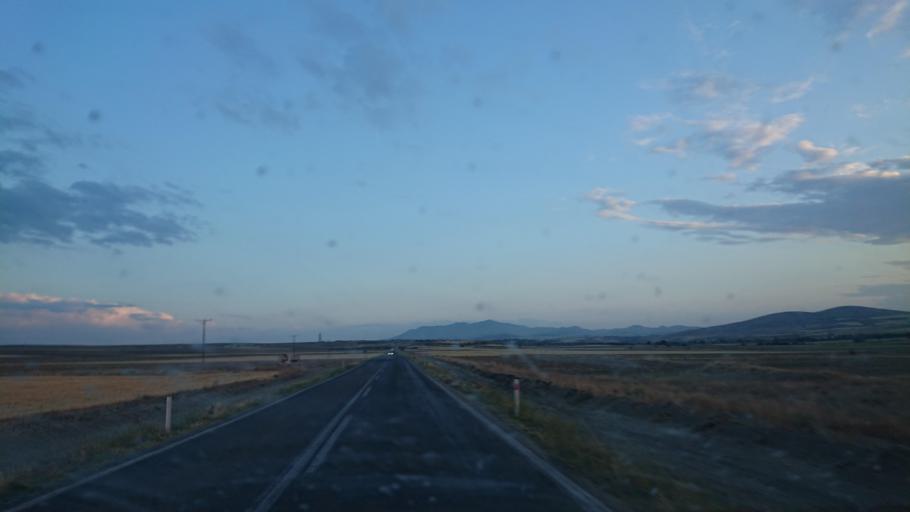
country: TR
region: Aksaray
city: Balci
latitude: 38.8178
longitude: 34.1346
